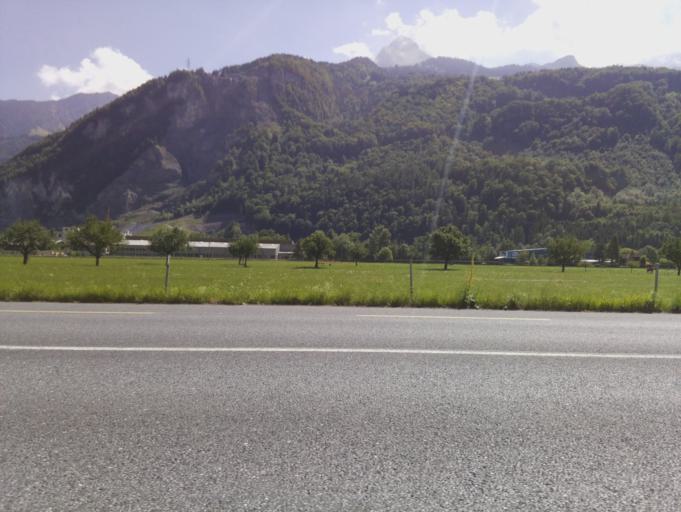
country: CH
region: Glarus
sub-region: Glarus
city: Netstal
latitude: 47.0721
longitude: 9.0563
